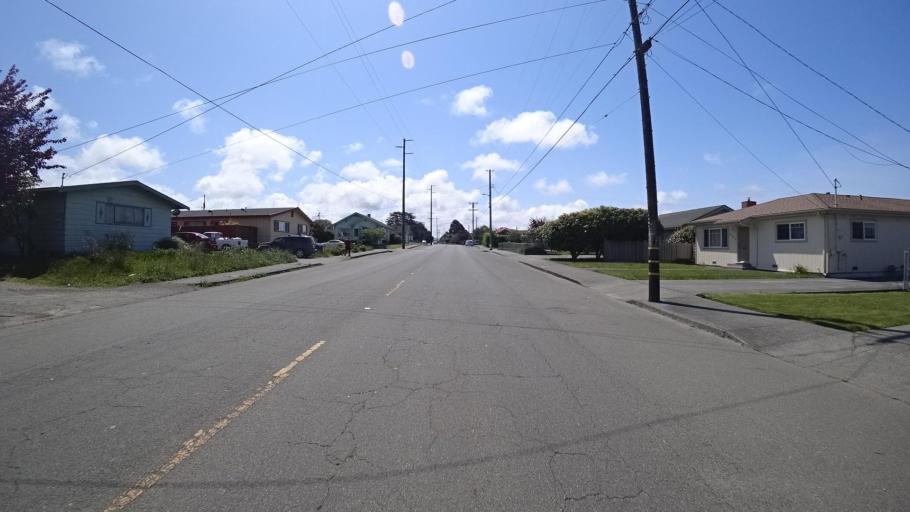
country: US
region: California
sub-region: Humboldt County
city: Bayview
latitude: 40.7789
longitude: -124.1803
